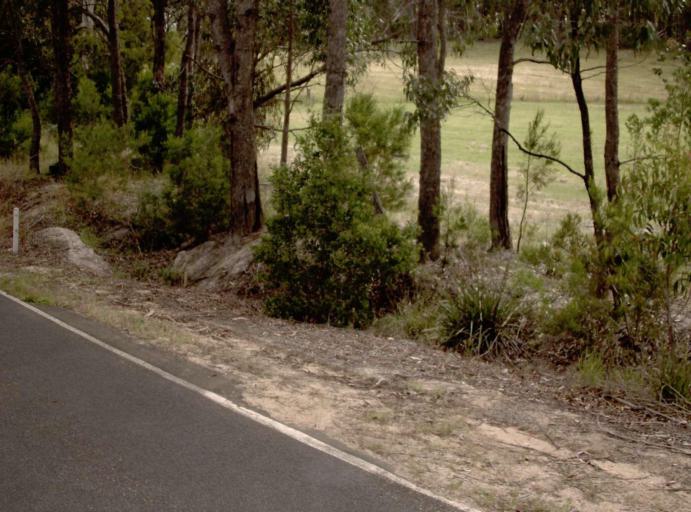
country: AU
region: Victoria
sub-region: Latrobe
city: Traralgon
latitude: -38.4066
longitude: 146.8241
